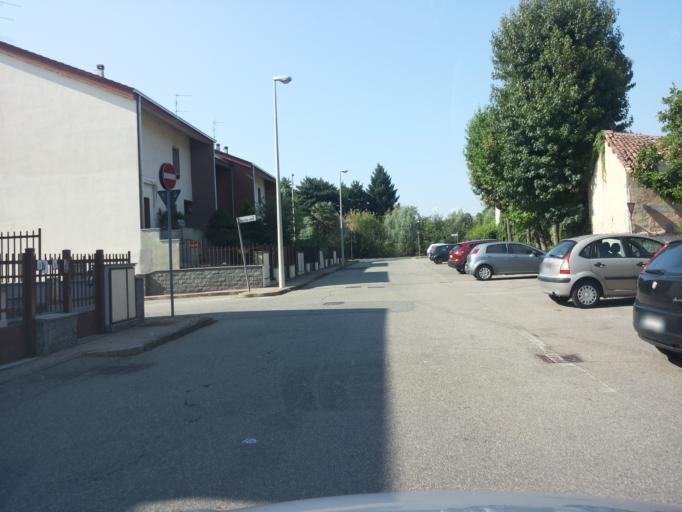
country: IT
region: Piedmont
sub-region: Provincia di Vercelli
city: Vercelli
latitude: 45.3164
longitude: 8.4040
